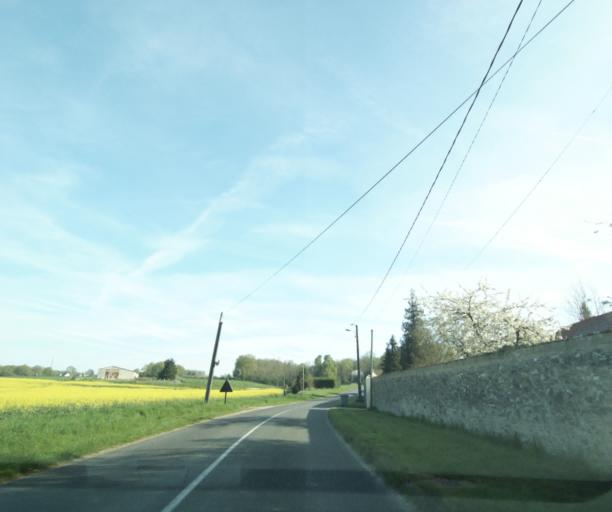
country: FR
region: Ile-de-France
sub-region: Departement de Seine-et-Marne
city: Vernou-la-Celle-sur-Seine
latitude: 48.4565
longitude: 2.8600
